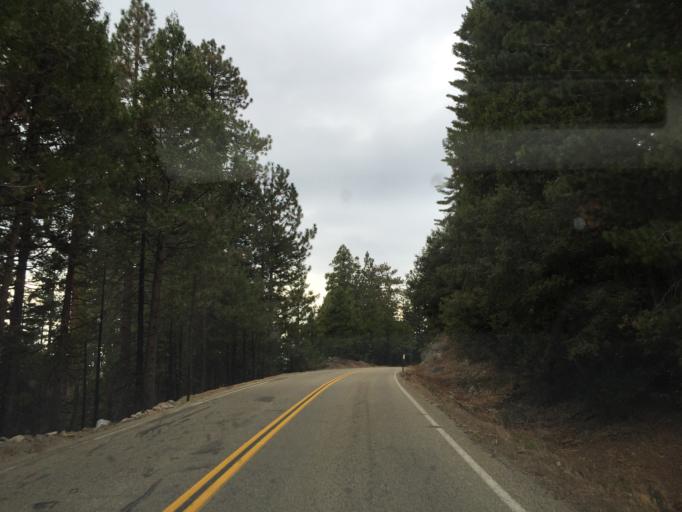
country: US
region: California
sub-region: Tulare County
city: Three Rivers
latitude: 36.7184
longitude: -118.9499
